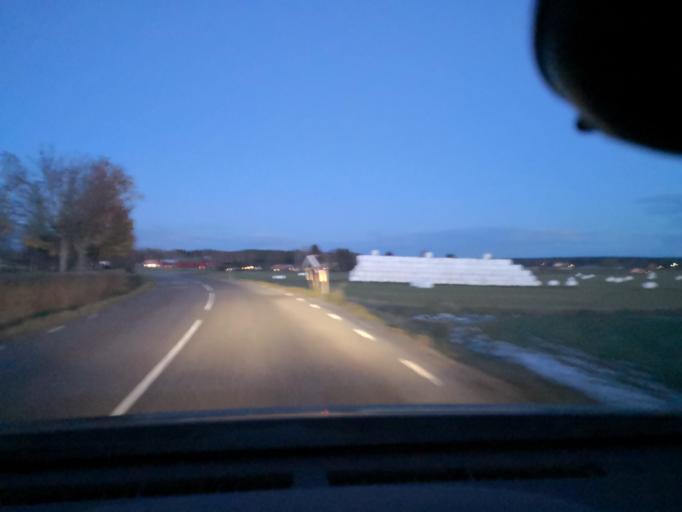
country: SE
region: Vaestmanland
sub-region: Sala Kommun
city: Sala
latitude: 59.8708
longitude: 16.7115
